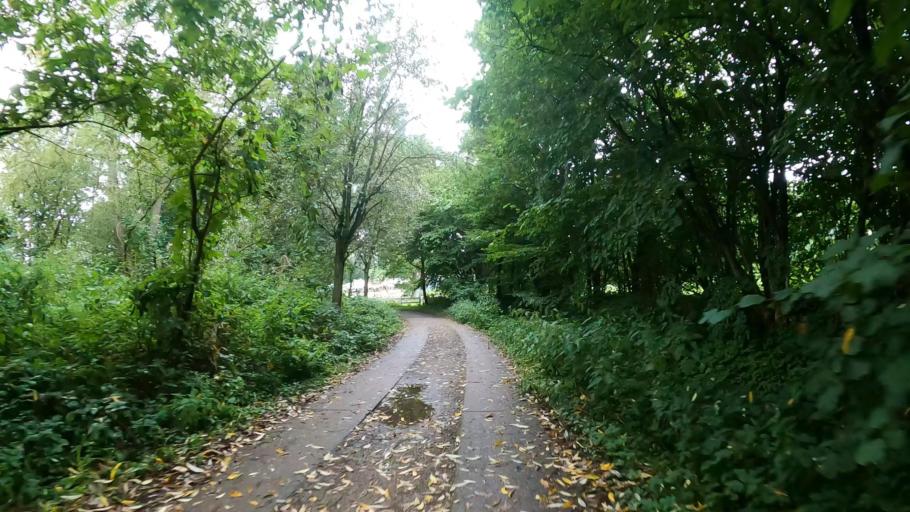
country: DE
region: Schleswig-Holstein
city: Pinneberg
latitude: 53.6678
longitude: 9.7672
